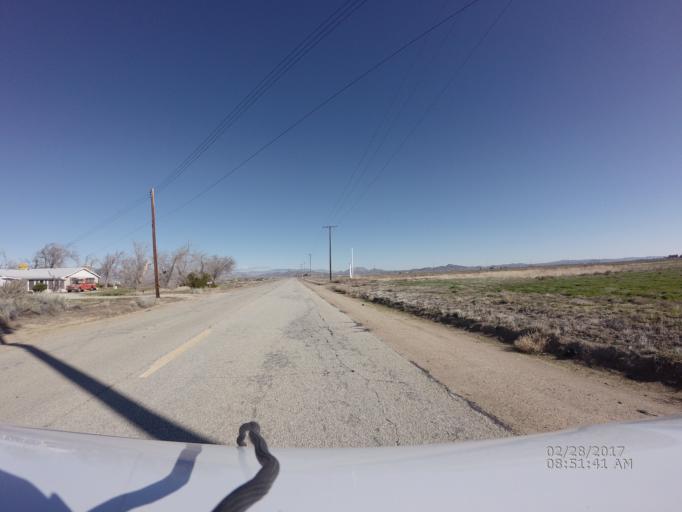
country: US
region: California
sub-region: Kern County
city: Rosamond
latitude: 34.8028
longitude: -118.2376
